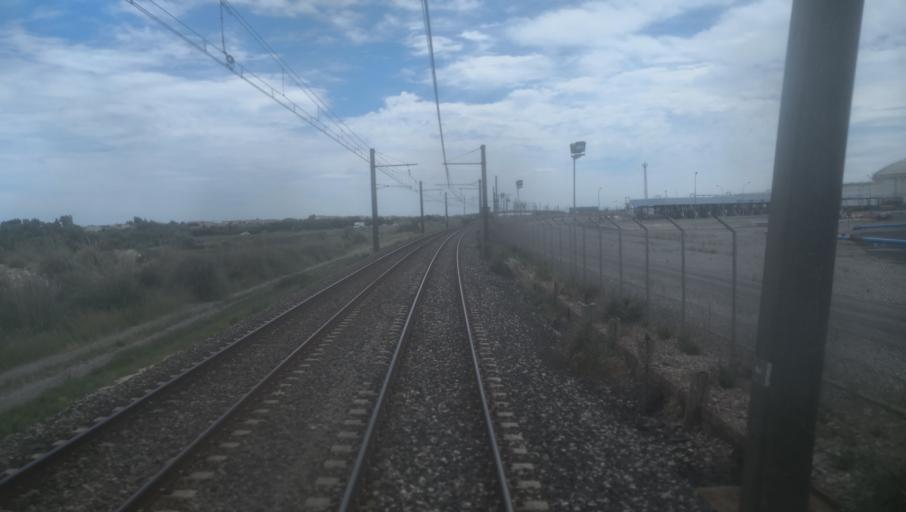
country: FR
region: Languedoc-Roussillon
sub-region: Departement de l'Herault
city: Frontignan
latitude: 43.4354
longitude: 3.7570
